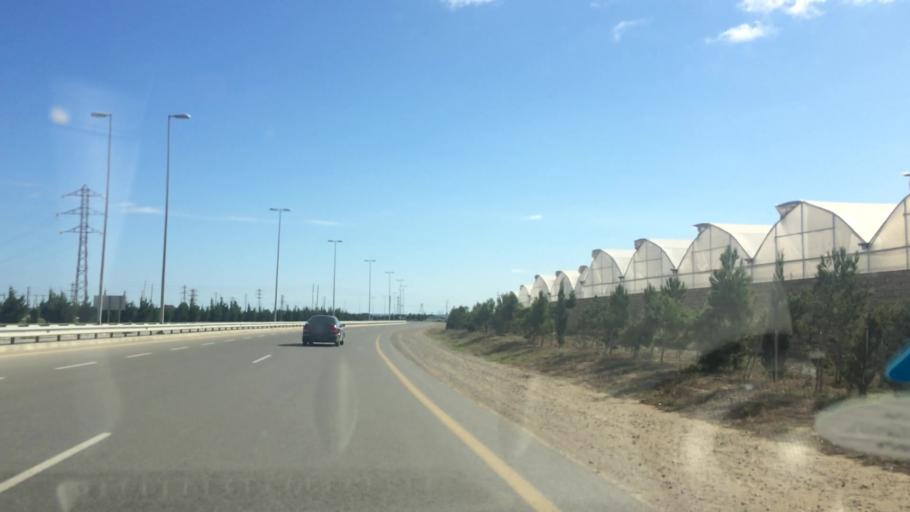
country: AZ
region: Baki
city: Zyrya
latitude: 40.3986
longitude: 50.3229
